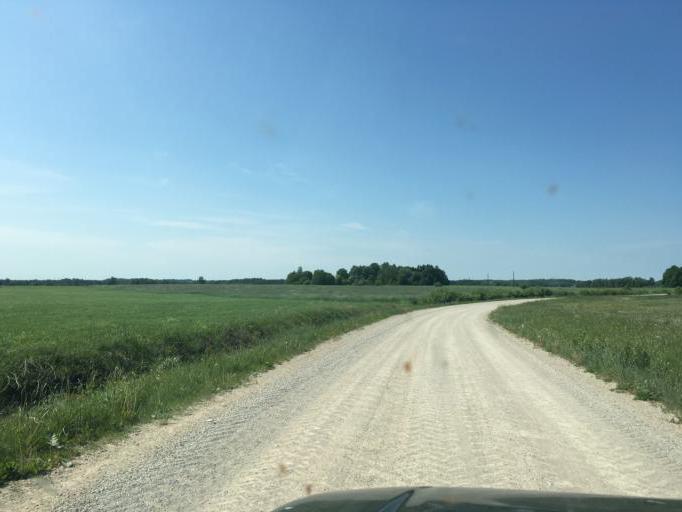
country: LV
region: Talsu Rajons
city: Valdemarpils
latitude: 57.4386
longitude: 22.5869
